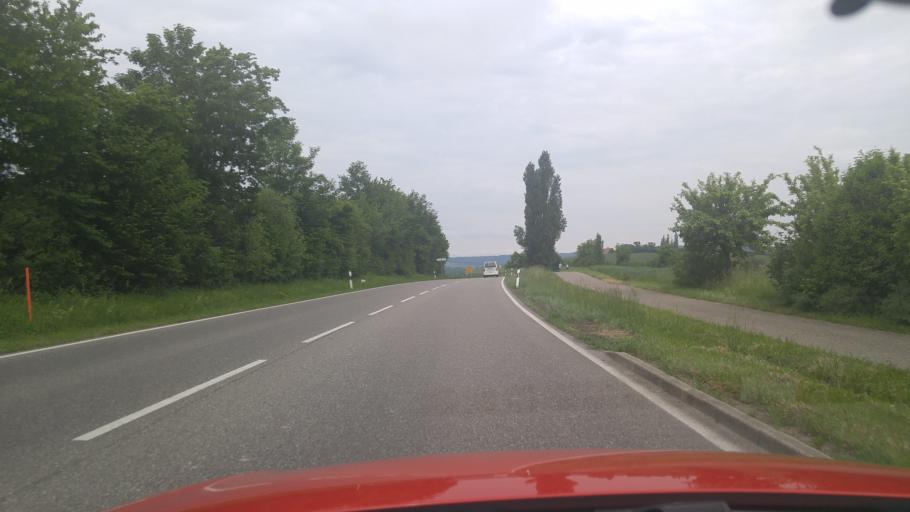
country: DE
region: Baden-Wuerttemberg
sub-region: Regierungsbezirk Stuttgart
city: Lowenstein
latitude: 49.1091
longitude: 9.3757
